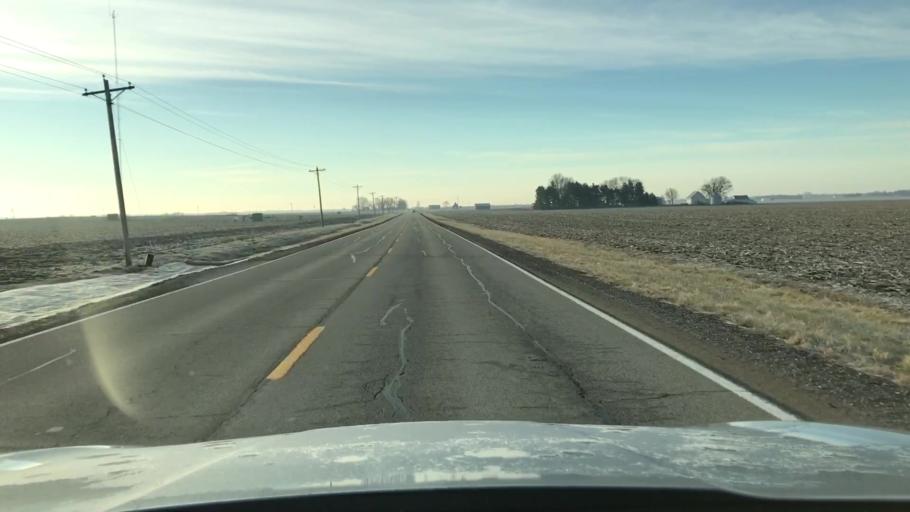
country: US
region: Illinois
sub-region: McLean County
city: Hudson
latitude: 40.5825
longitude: -88.9448
